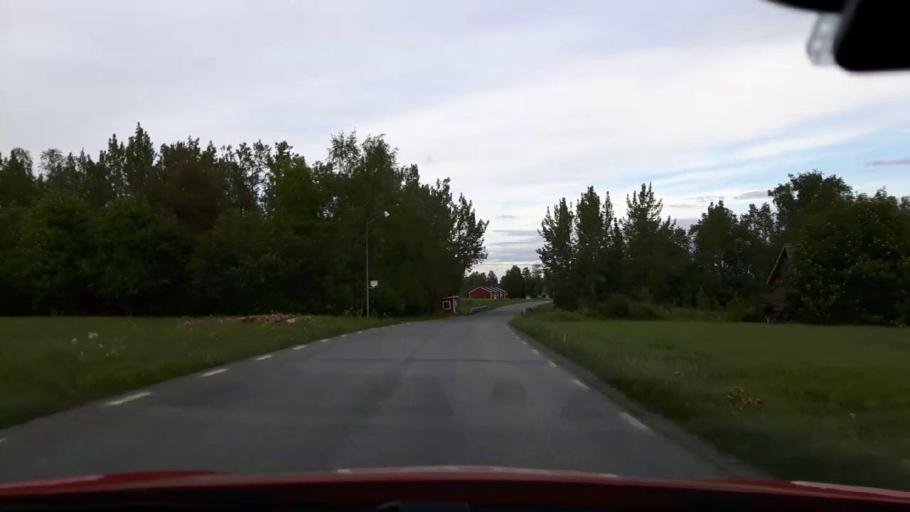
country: SE
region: Jaemtland
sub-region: OEstersunds Kommun
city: Ostersund
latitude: 63.0456
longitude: 14.4546
